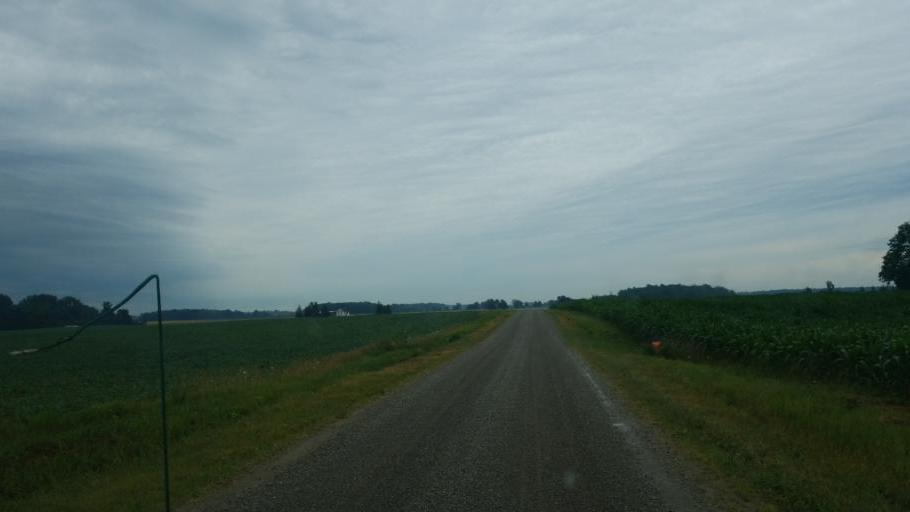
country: US
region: Indiana
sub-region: DeKalb County
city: Butler
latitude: 41.4472
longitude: -84.9098
